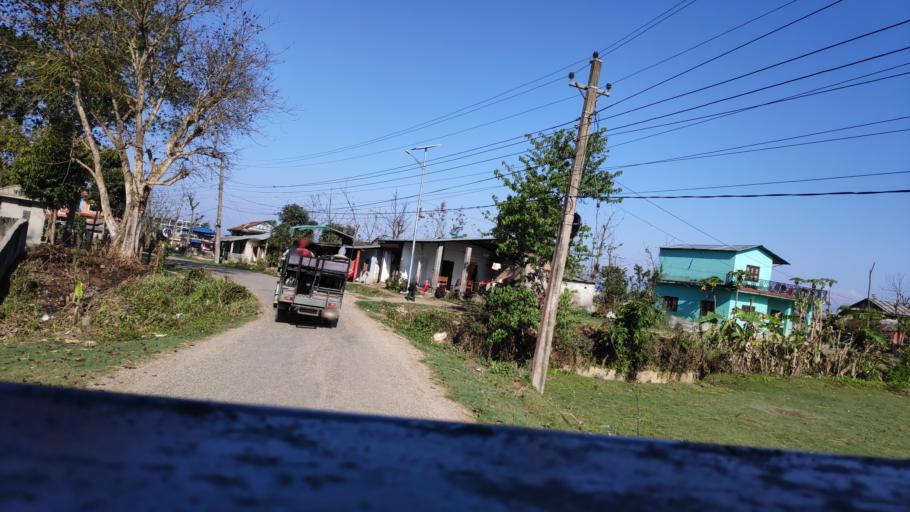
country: NP
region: Central Region
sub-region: Narayani Zone
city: Bharatpur
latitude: 27.5760
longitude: 84.5057
